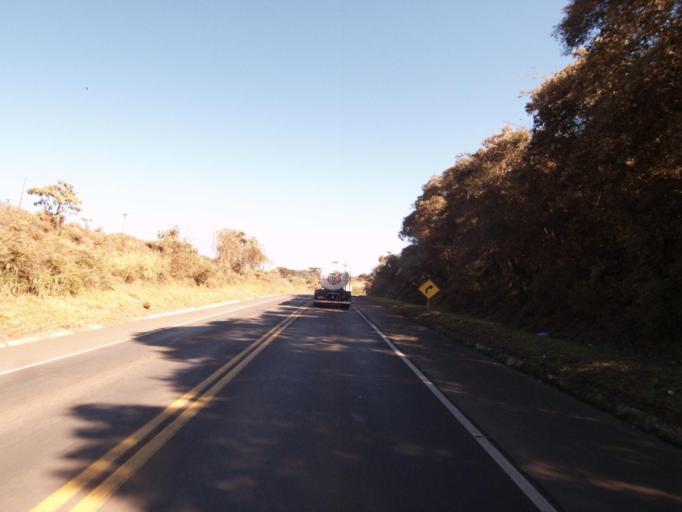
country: BR
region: Santa Catarina
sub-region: Xanxere
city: Xanxere
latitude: -26.8715
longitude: -52.3188
